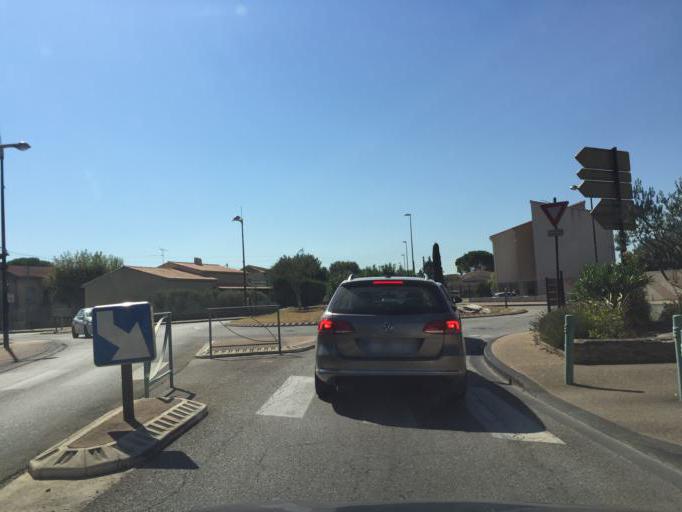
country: FR
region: Provence-Alpes-Cote d'Azur
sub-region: Departement du Vaucluse
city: Vedene
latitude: 43.9776
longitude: 4.9088
